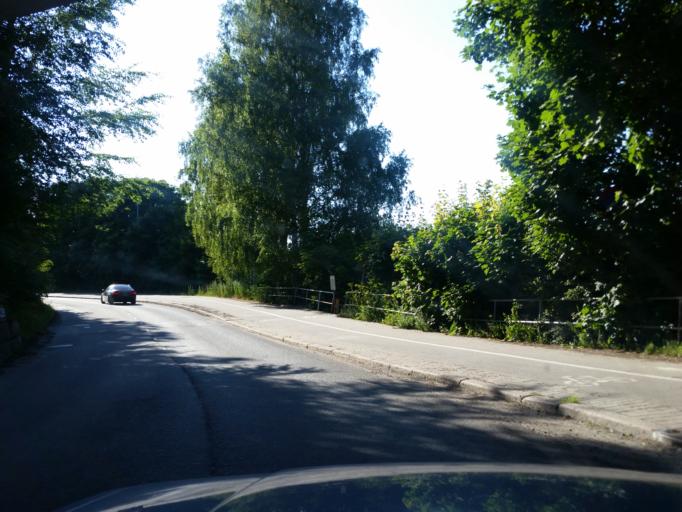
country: FI
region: Uusimaa
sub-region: Helsinki
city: Helsinki
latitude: 60.1922
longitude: 25.0218
